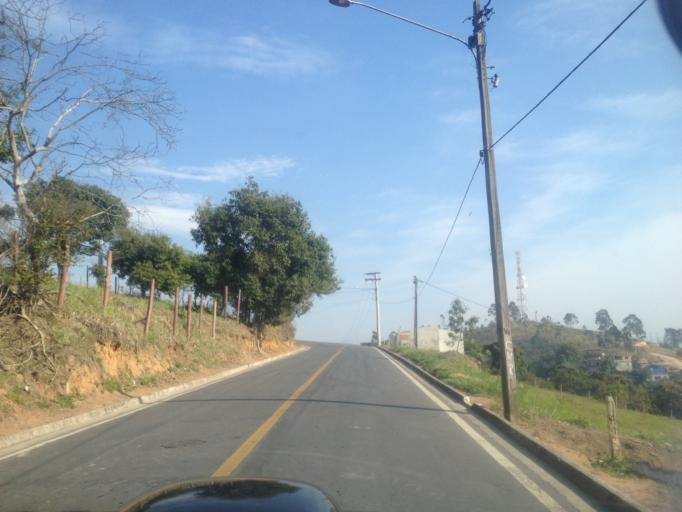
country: BR
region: Rio de Janeiro
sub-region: Porto Real
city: Porto Real
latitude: -22.4424
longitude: -44.3175
